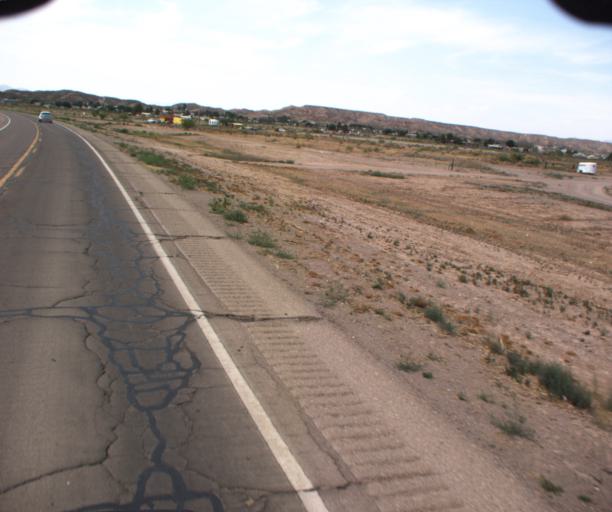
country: US
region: Arizona
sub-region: Greenlee County
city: Clifton
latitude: 32.7396
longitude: -109.0949
